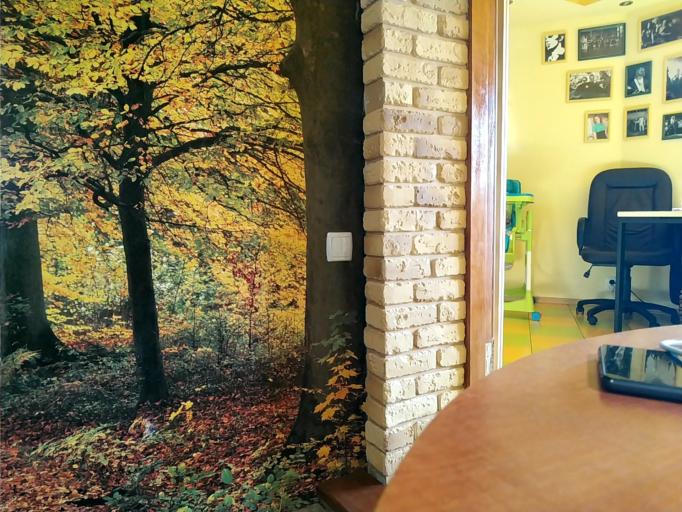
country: RU
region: Leningrad
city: Volosovo
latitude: 59.0306
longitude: 29.2875
